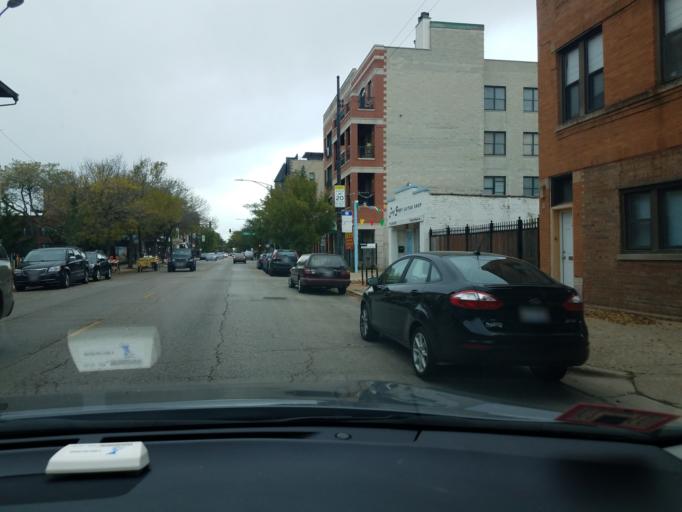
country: US
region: Illinois
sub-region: Cook County
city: Lincolnwood
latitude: 41.9397
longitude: -87.6748
